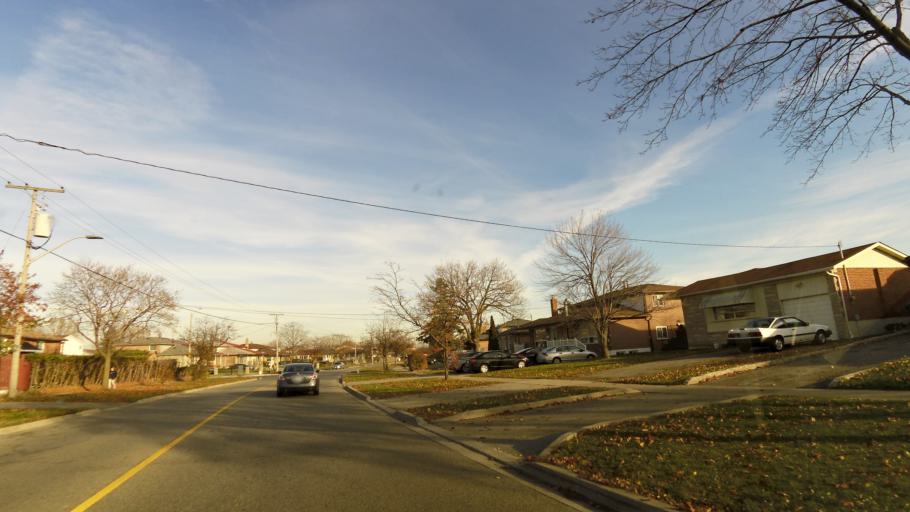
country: CA
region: Ontario
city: Etobicoke
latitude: 43.7255
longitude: -79.6308
